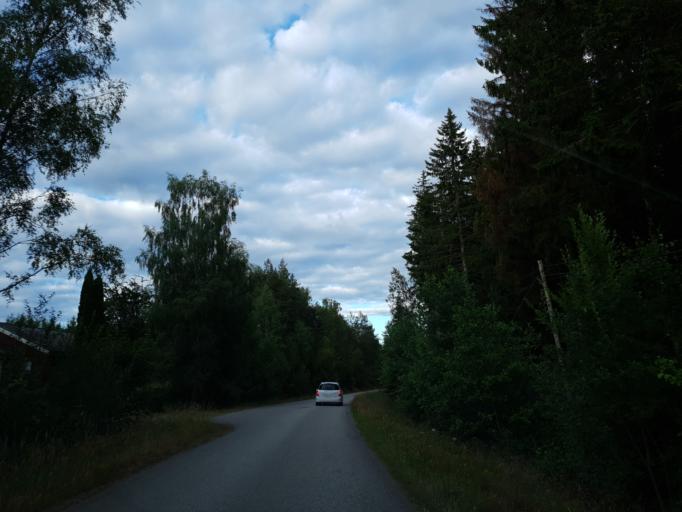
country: SE
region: Kalmar
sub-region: Emmaboda Kommun
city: Emmaboda
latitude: 56.6235
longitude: 15.6597
